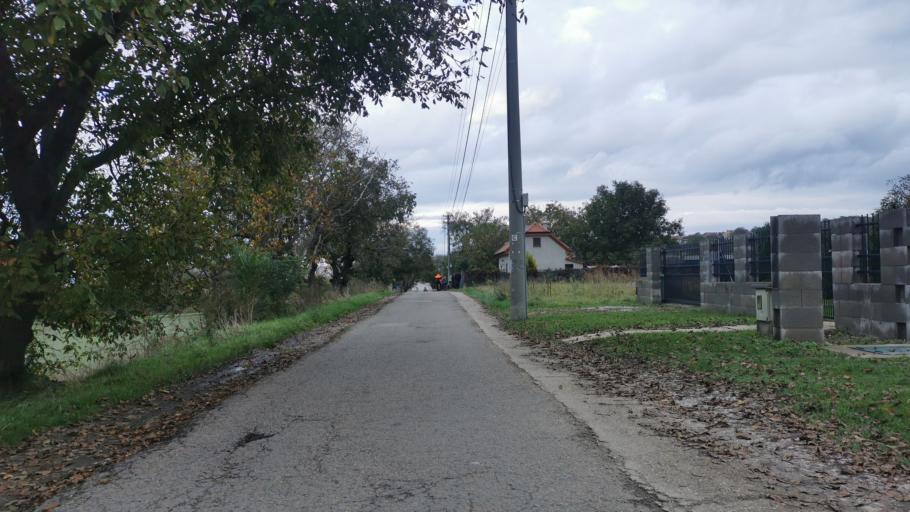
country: SK
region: Trnavsky
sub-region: Okres Skalica
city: Skalica
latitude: 48.8252
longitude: 17.2226
